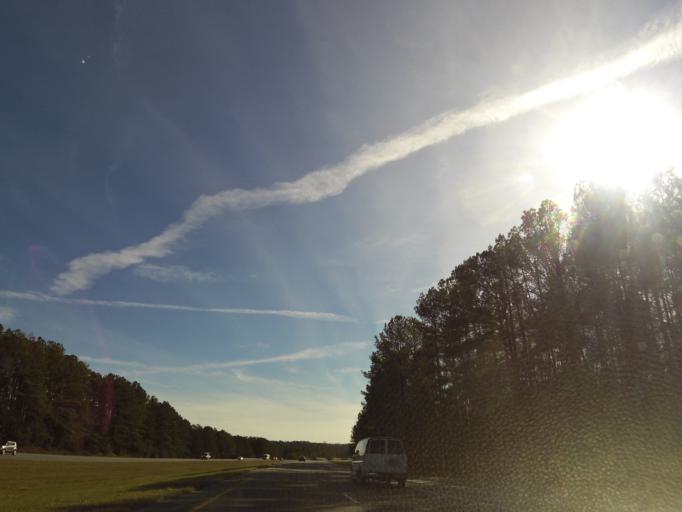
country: US
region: Alabama
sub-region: Russell County
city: Phenix City
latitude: 32.6117
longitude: -84.9506
